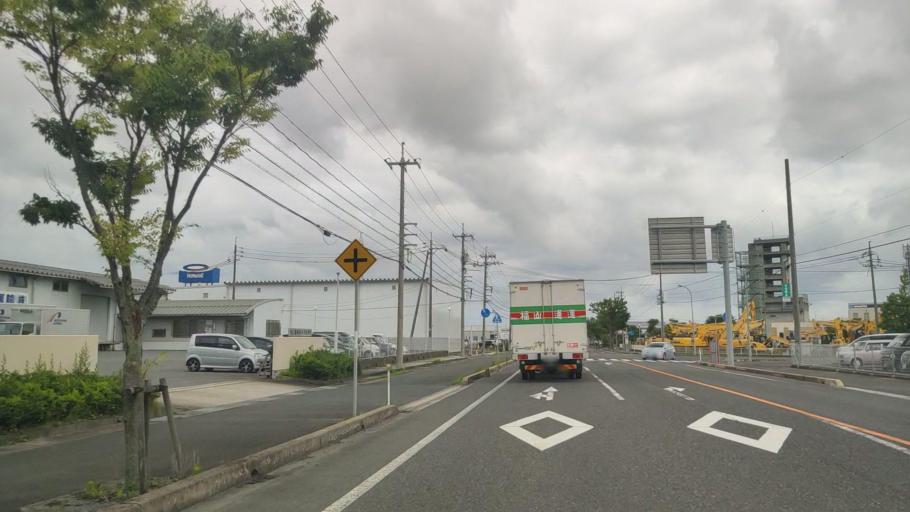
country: JP
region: Tottori
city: Yonago
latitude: 35.4270
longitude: 133.3954
